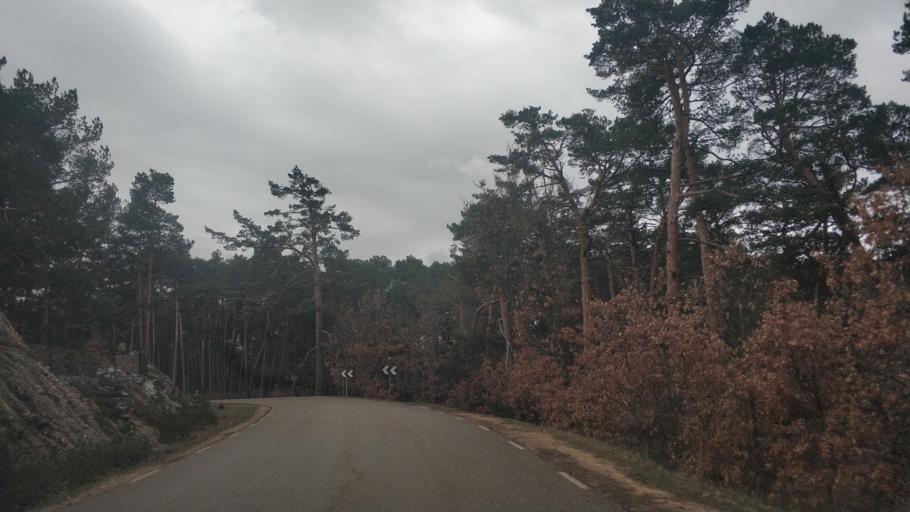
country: ES
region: Castille and Leon
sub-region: Provincia de Burgos
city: Canicosa de la Sierra
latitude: 41.9216
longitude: -3.0385
